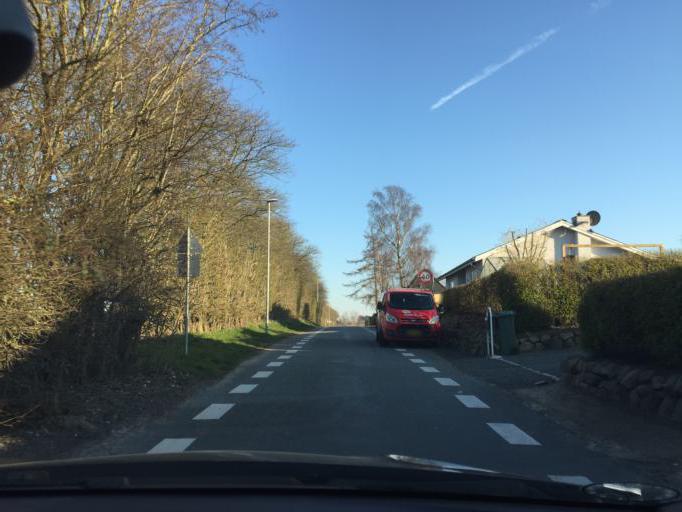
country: DK
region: South Denmark
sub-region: Faaborg-Midtfyn Kommune
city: Arslev
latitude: 55.2972
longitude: 10.4671
